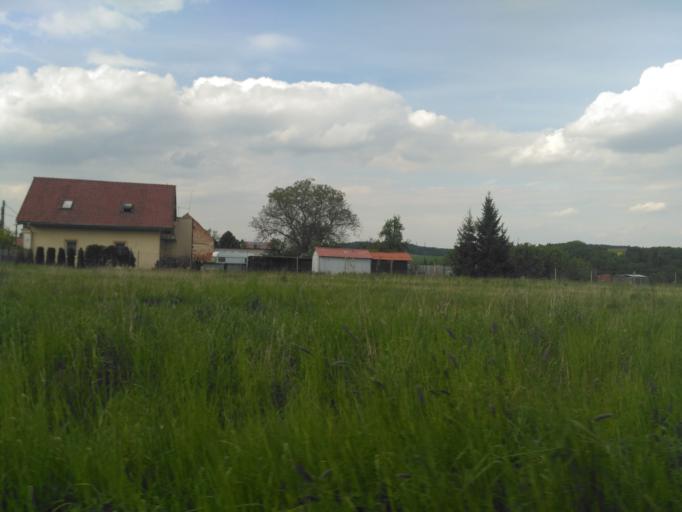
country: CZ
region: Central Bohemia
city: Chynava
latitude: 50.0070
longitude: 14.0920
